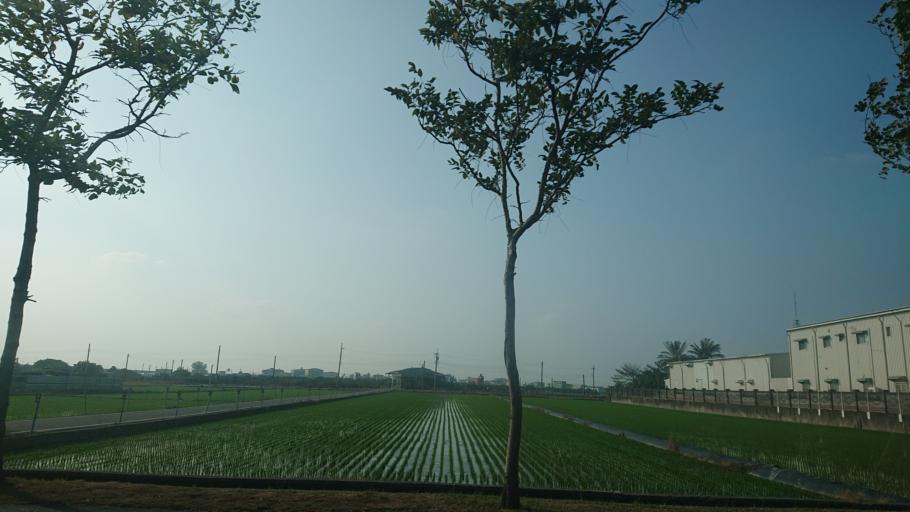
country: TW
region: Taiwan
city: Xinying
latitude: 23.2046
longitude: 120.2711
